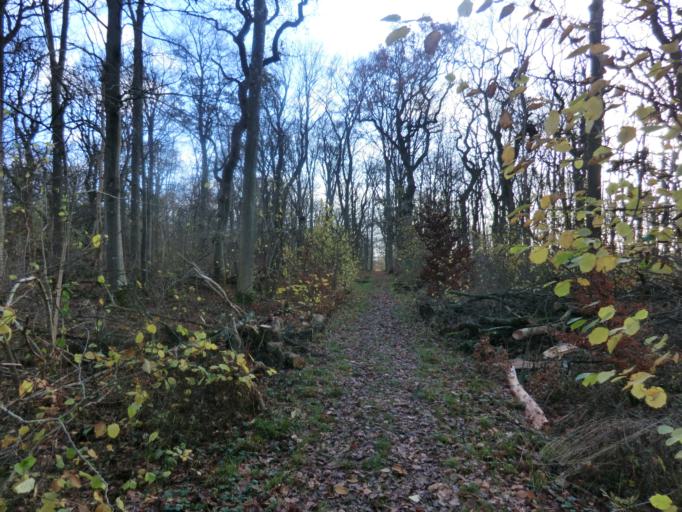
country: SE
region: Skane
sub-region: Lunds Kommun
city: Genarp
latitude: 55.6757
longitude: 13.3294
